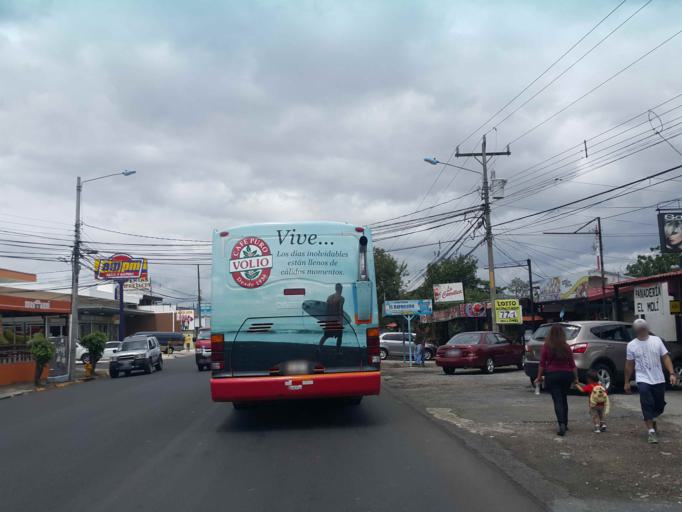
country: CR
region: Heredia
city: Heredia
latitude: 10.0135
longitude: -84.1208
